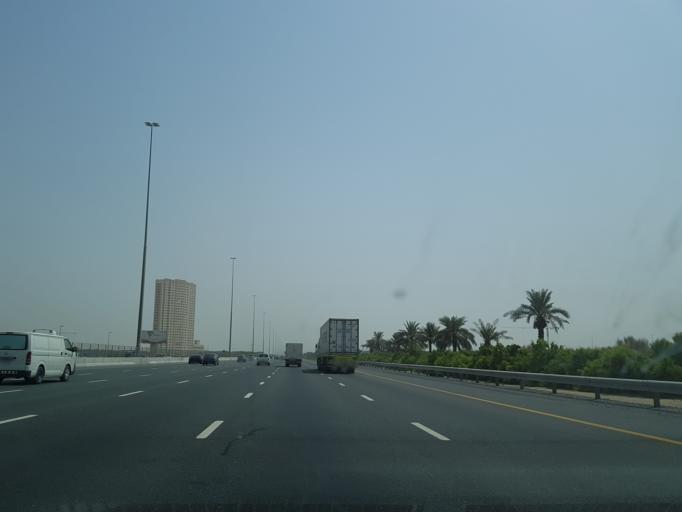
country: AE
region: Dubai
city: Dubai
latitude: 25.0875
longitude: 55.3198
